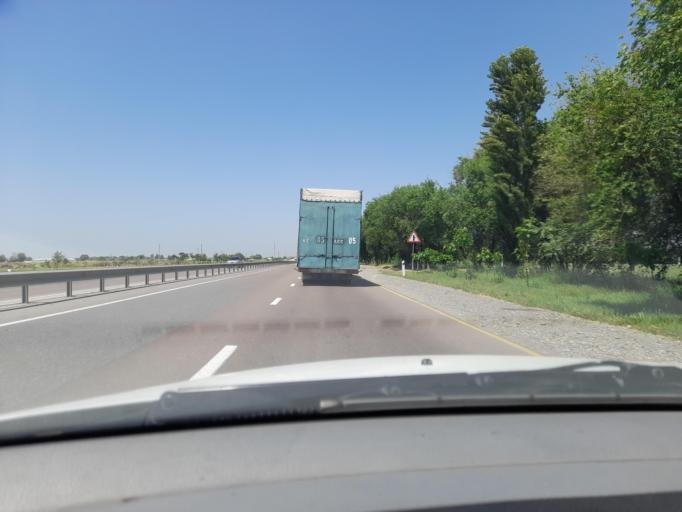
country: KZ
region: Ongtustik Qazaqstan
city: Myrzakent
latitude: 40.5314
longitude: 68.4376
